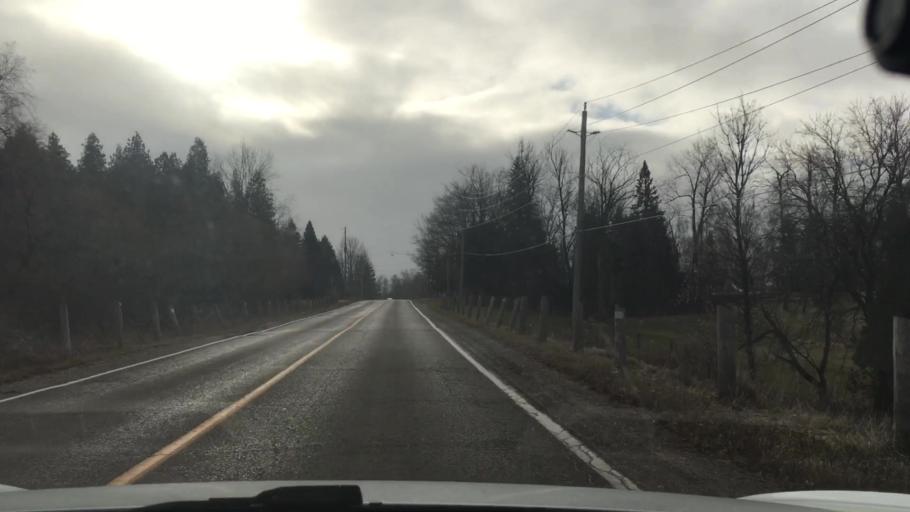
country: CA
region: Ontario
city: Oshawa
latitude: 43.9349
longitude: -78.7990
